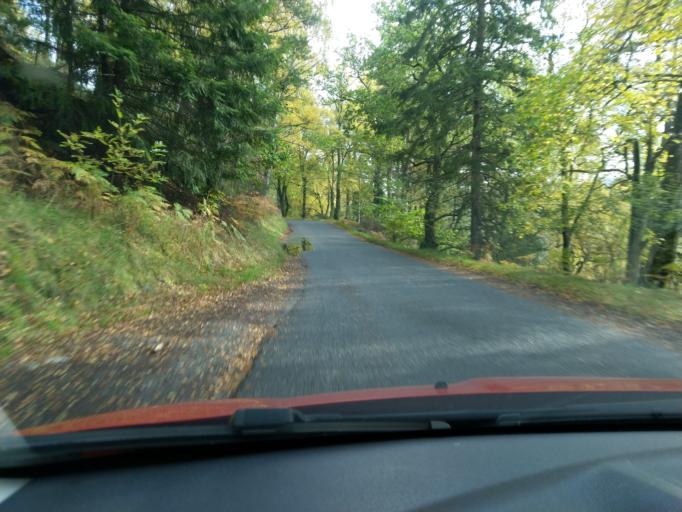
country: GB
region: Scotland
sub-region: Perth and Kinross
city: Aberfeldy
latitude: 56.7070
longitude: -4.0898
